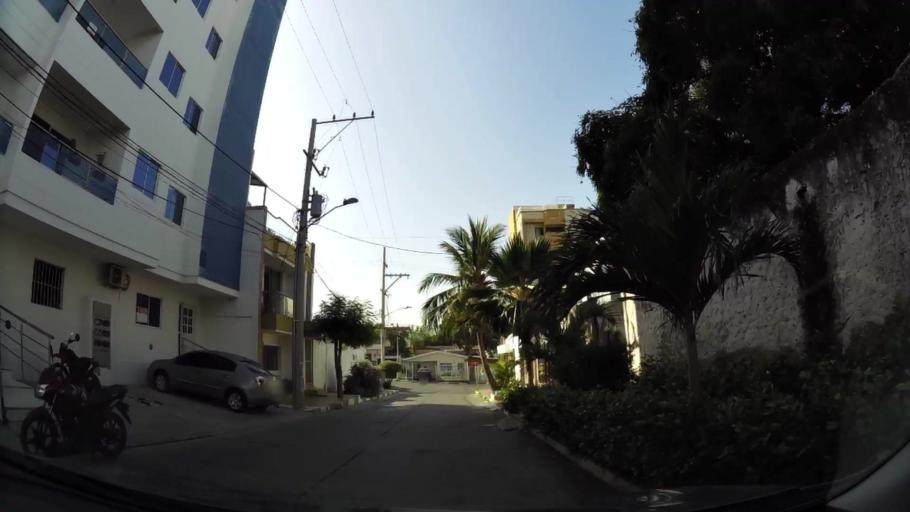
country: CO
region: Bolivar
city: Cartagena
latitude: 10.3906
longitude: -75.5182
